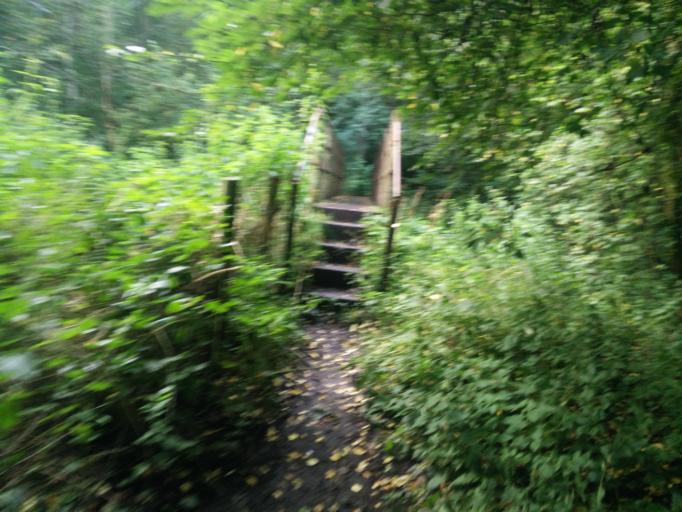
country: GB
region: England
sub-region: County Durham
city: Crook
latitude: 54.7234
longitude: -1.7606
